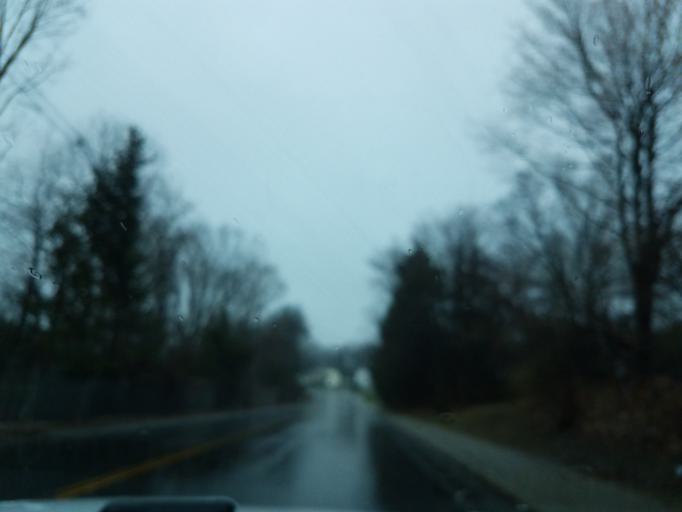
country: US
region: Connecticut
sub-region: New Haven County
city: Waterbury
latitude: 41.5368
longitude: -73.0665
